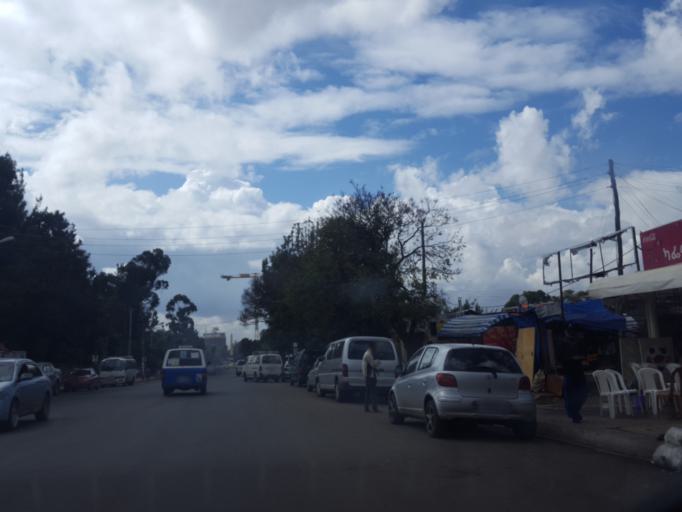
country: ET
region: Adis Abeba
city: Addis Ababa
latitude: 9.0490
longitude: 38.7619
